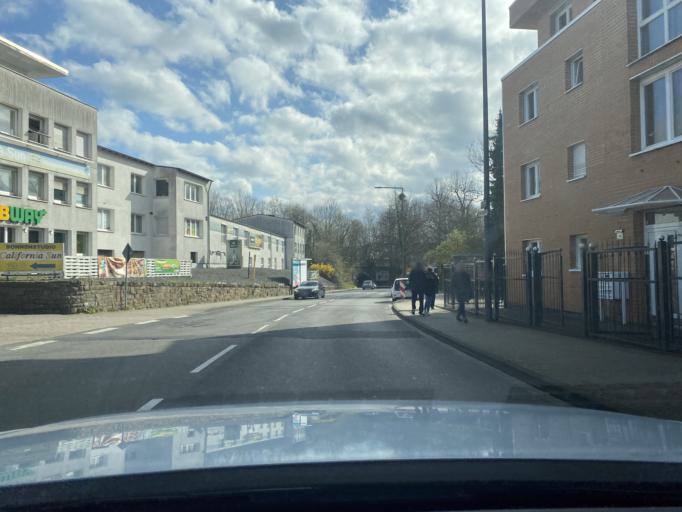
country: DE
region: North Rhine-Westphalia
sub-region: Regierungsbezirk Koln
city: Bergisch Gladbach
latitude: 50.9841
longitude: 7.1167
